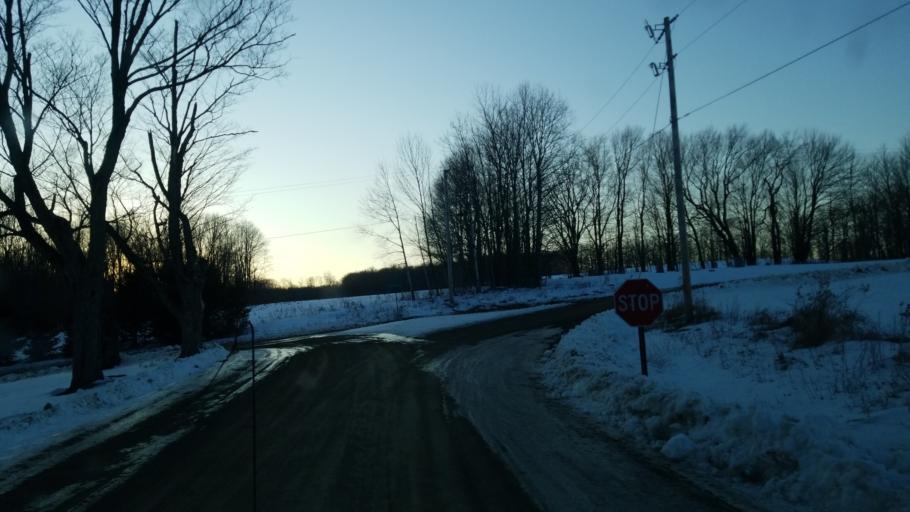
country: US
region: Pennsylvania
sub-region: Tioga County
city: Westfield
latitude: 42.0396
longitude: -77.6190
